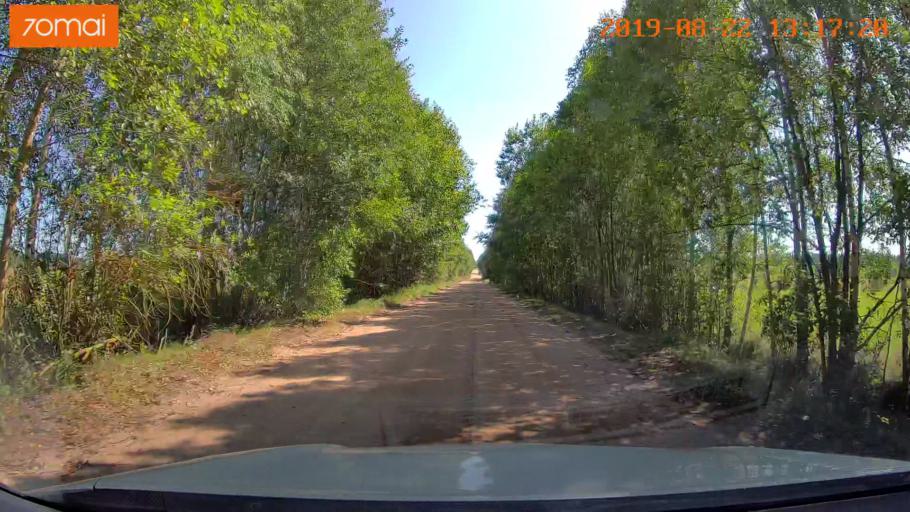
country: BY
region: Minsk
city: Prawdzinski
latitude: 53.2490
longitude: 27.9206
